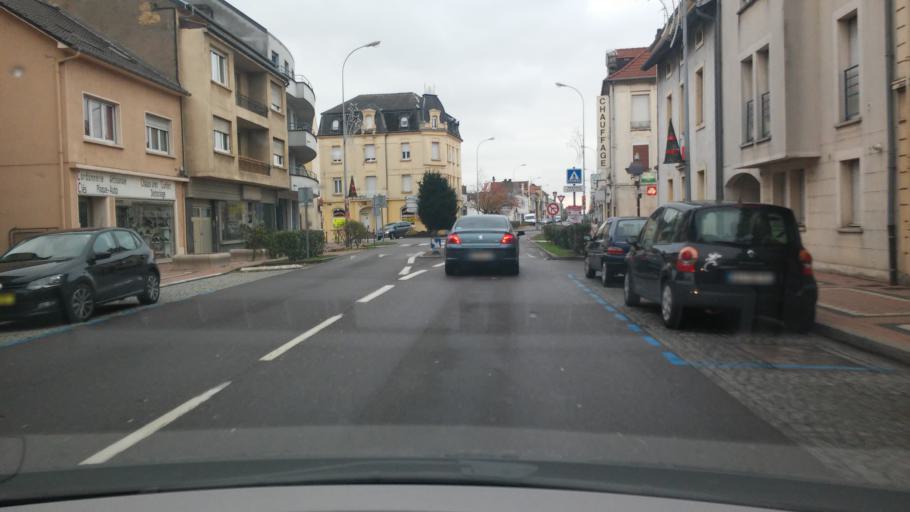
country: FR
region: Lorraine
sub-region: Departement de la Moselle
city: Hagondange
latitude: 49.2494
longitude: 6.1700
